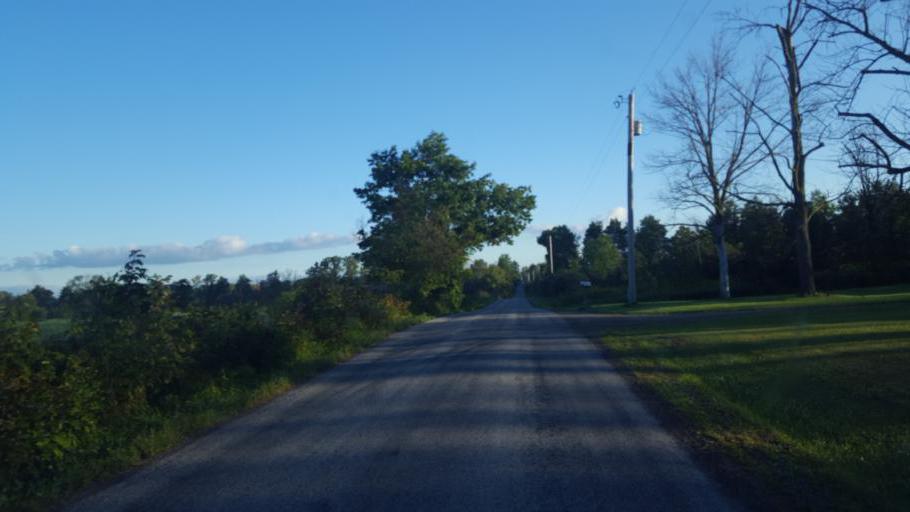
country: US
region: Ohio
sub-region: Wayne County
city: West Salem
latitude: 40.9940
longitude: -82.2423
